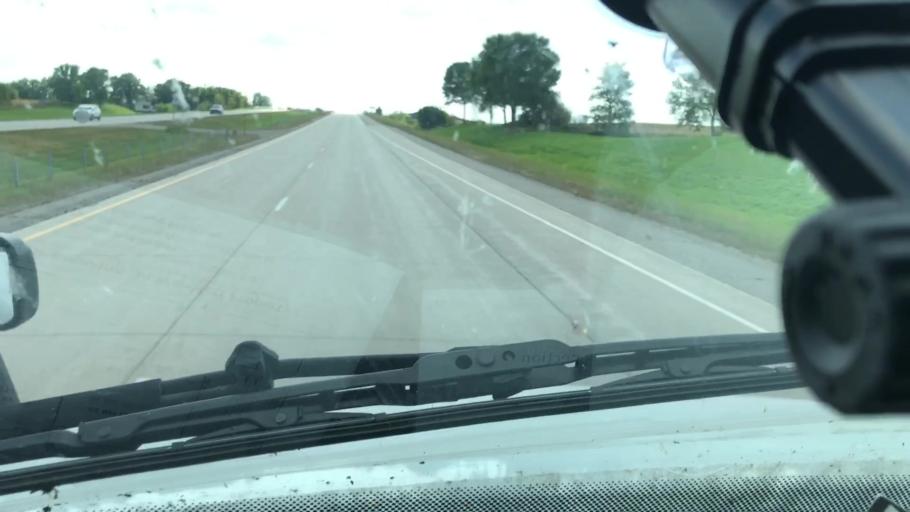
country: US
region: Minnesota
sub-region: Freeborn County
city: Albert Lea
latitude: 43.6544
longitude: -93.3211
